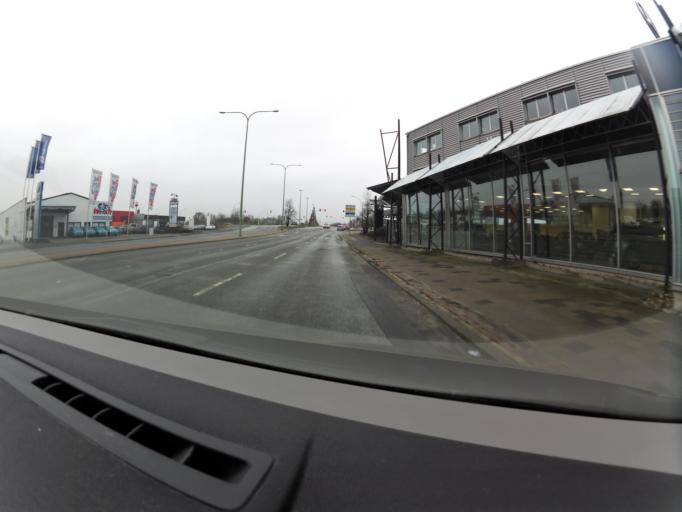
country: DE
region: Bremen
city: Bremerhaven
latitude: 53.5490
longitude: 8.5942
